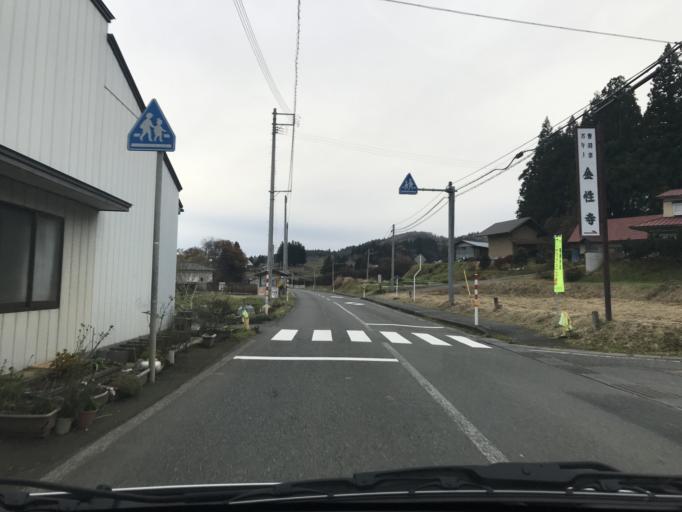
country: JP
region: Iwate
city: Kitakami
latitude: 39.2805
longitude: 141.2665
